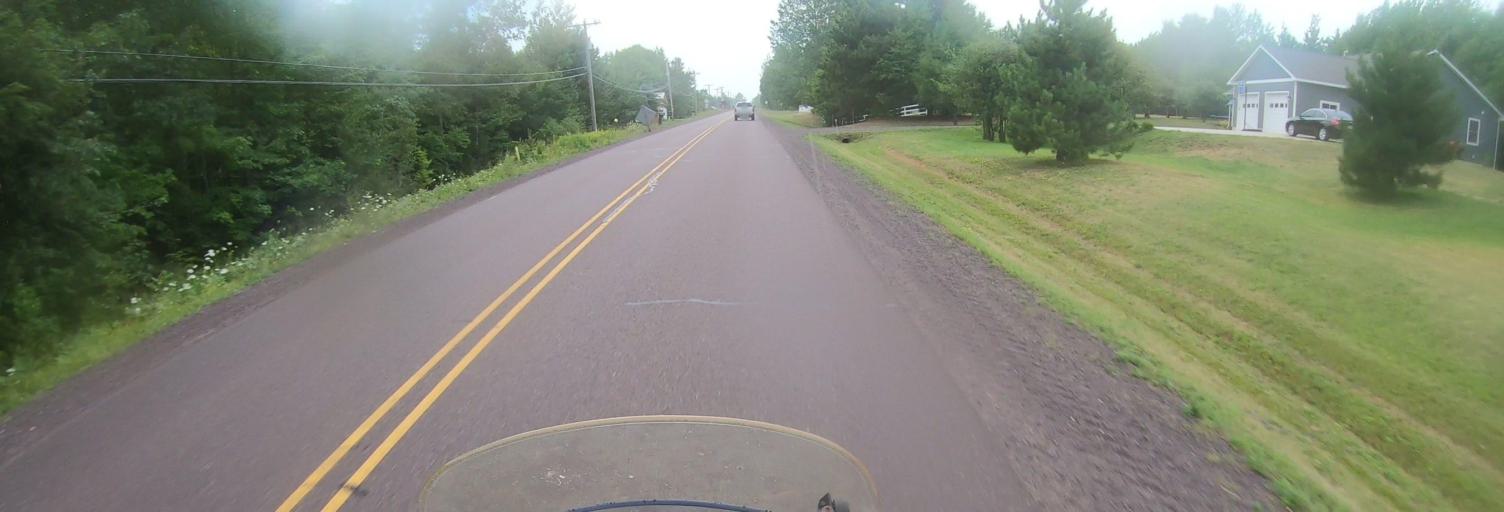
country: US
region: Michigan
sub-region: Houghton County
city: Dollar Bay
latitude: 47.0260
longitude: -88.5395
